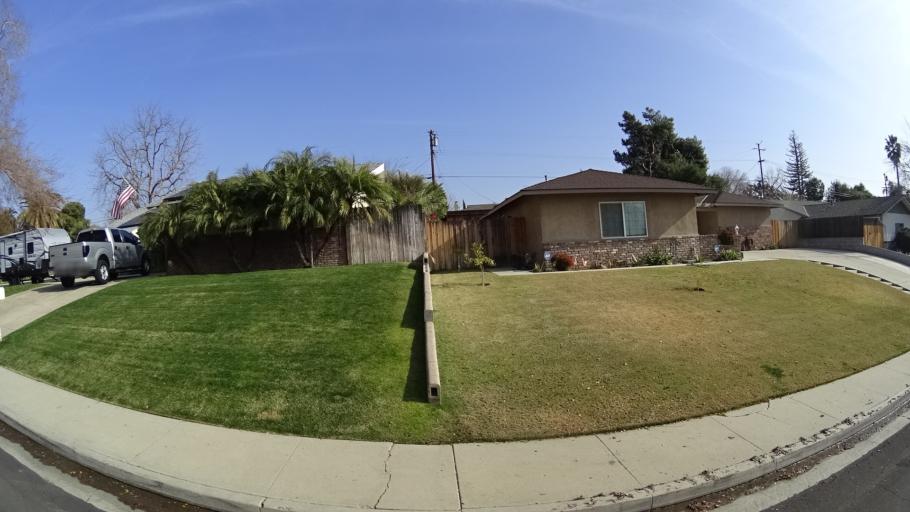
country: US
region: California
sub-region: Kern County
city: Bakersfield
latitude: 35.3878
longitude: -118.9490
